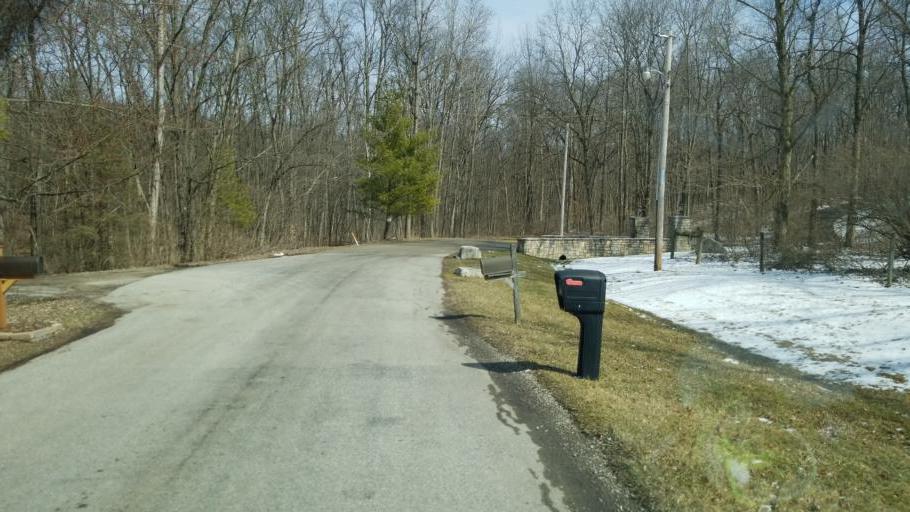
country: US
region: Ohio
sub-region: Delaware County
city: Sunbury
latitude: 40.3038
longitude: -82.8443
